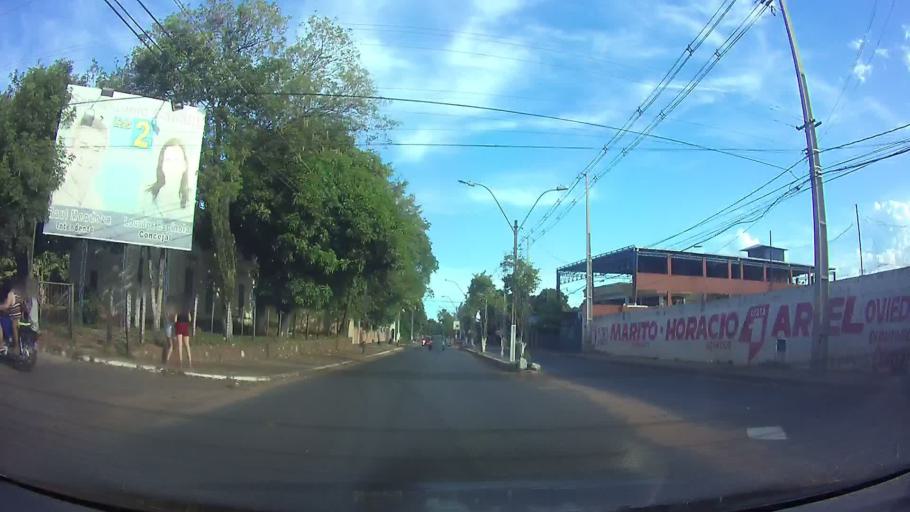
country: PY
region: Central
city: San Antonio
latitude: -25.4253
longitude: -57.5586
